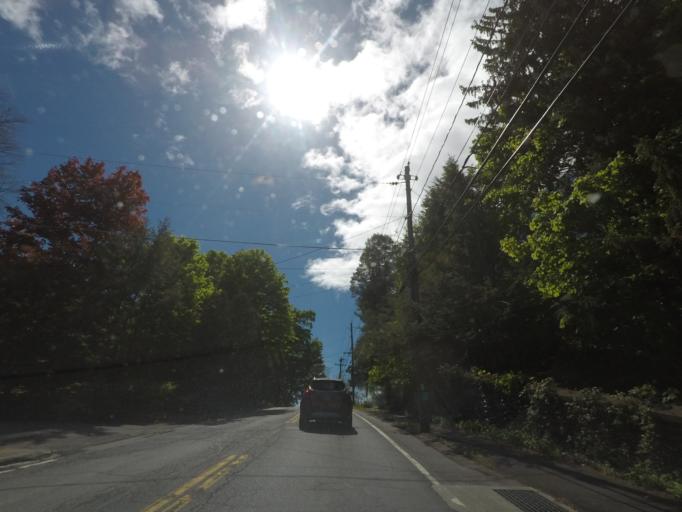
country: US
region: New York
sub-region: Ulster County
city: Saugerties South
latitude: 42.0698
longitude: -73.9478
